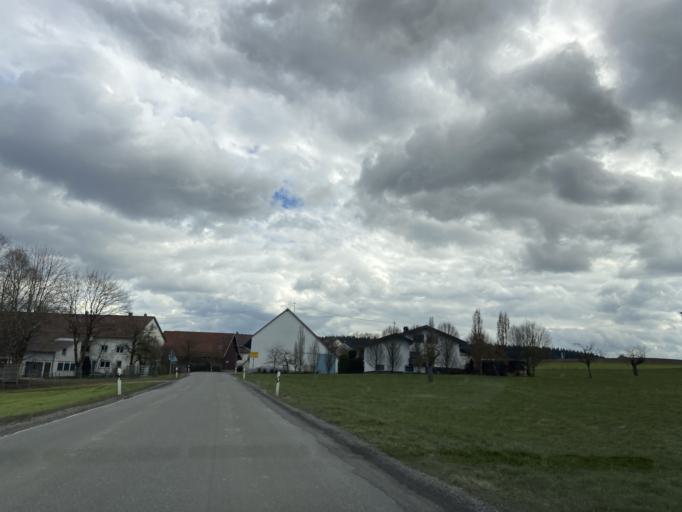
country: DE
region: Baden-Wuerttemberg
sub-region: Tuebingen Region
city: Ostrach
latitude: 47.9422
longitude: 9.3996
